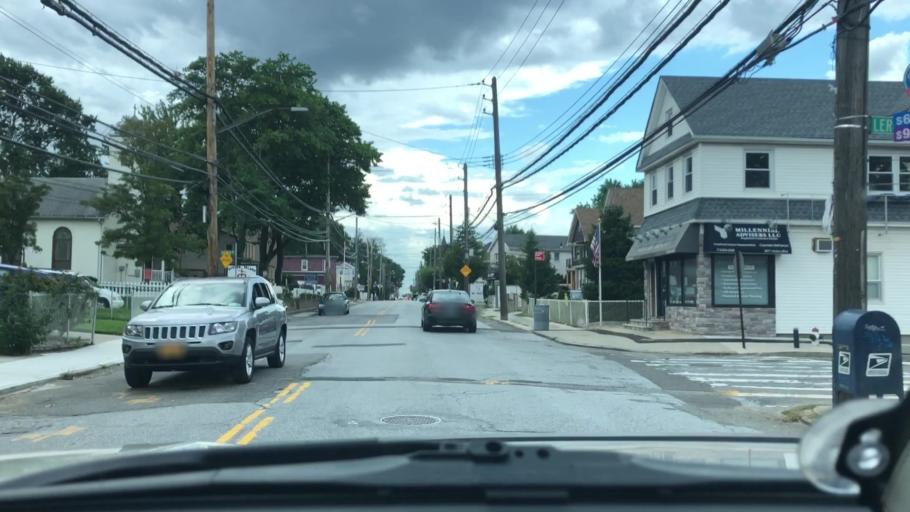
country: US
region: New York
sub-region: Richmond County
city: Bloomfield
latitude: 40.5942
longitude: -74.1865
